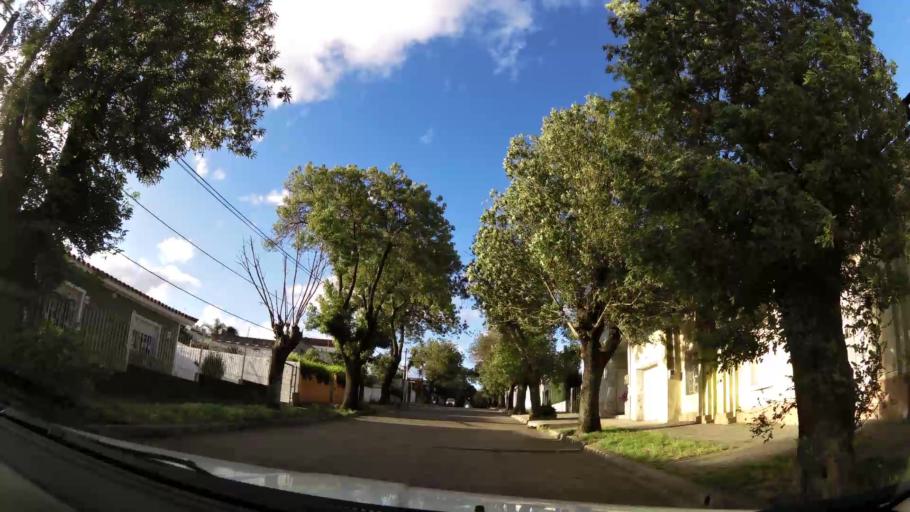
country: UY
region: Montevideo
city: Montevideo
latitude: -34.8939
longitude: -56.2496
